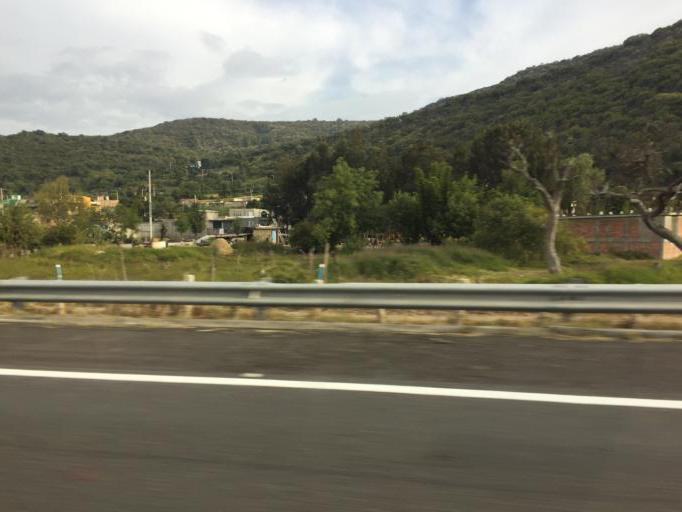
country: MX
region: Michoacan
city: Copandaro de Galeana
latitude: 19.8820
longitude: -101.1993
